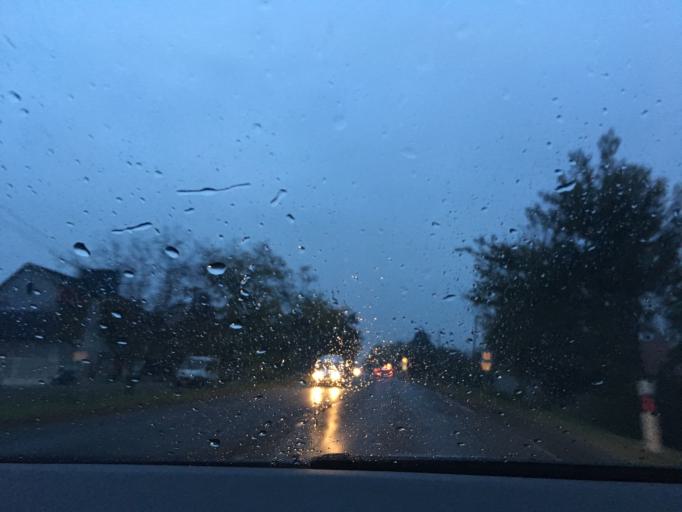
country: HU
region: Pest
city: Nyaregyhaza
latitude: 47.3076
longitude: 19.5018
